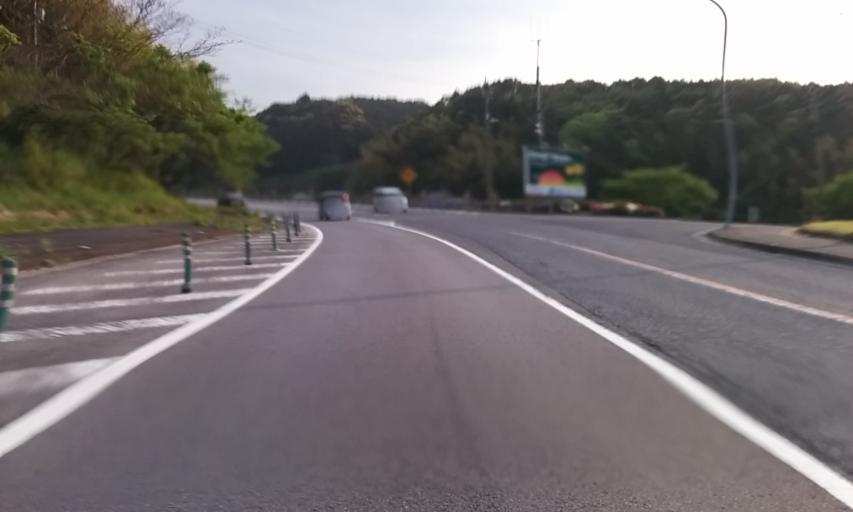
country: JP
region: Ehime
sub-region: Shikoku-chuo Shi
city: Matsuyama
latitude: 33.8055
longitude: 132.9706
